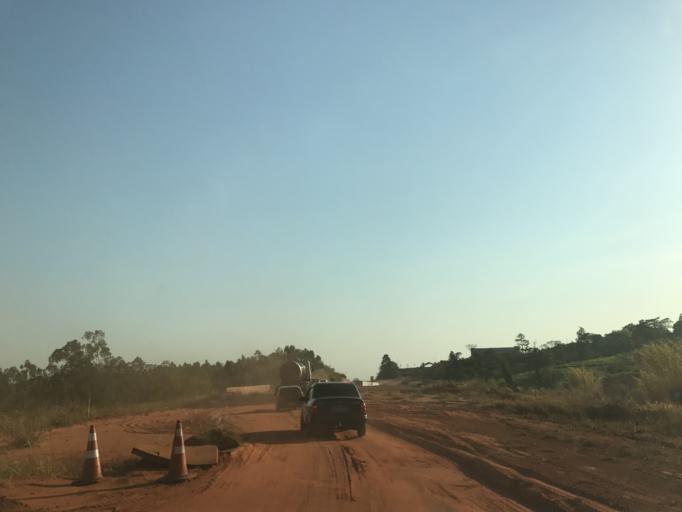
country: BR
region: Sao Paulo
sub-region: Marilia
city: Marilia
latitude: -22.1145
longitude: -49.9277
